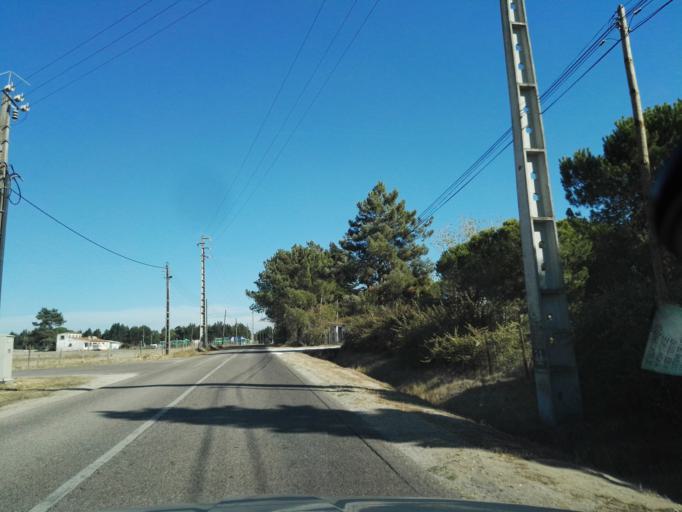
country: PT
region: Santarem
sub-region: Benavente
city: Benavente
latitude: 38.9394
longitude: -8.7966
